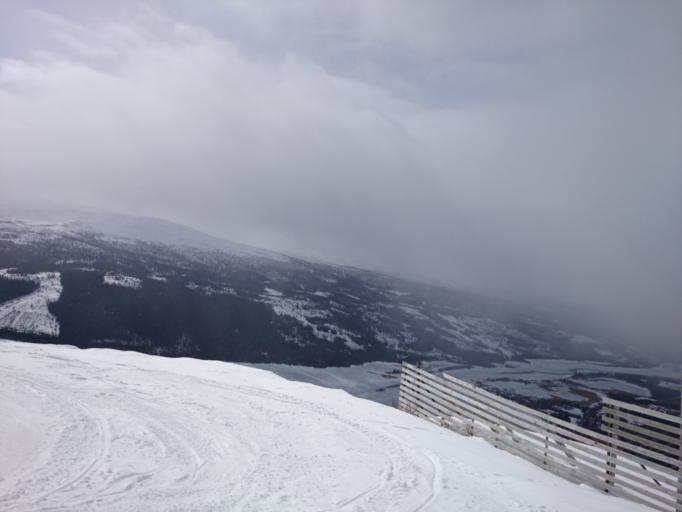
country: SE
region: Jaemtland
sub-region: Are Kommun
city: Are
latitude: 63.4128
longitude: 13.0765
